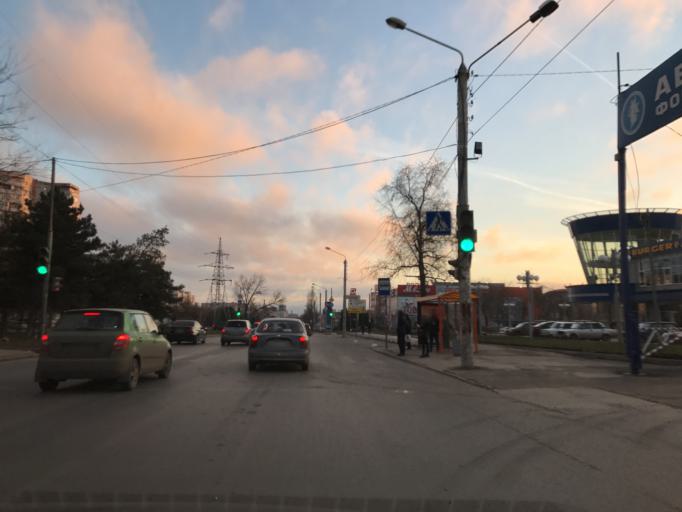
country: RU
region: Rostov
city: Kalinin
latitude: 47.2333
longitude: 39.6134
